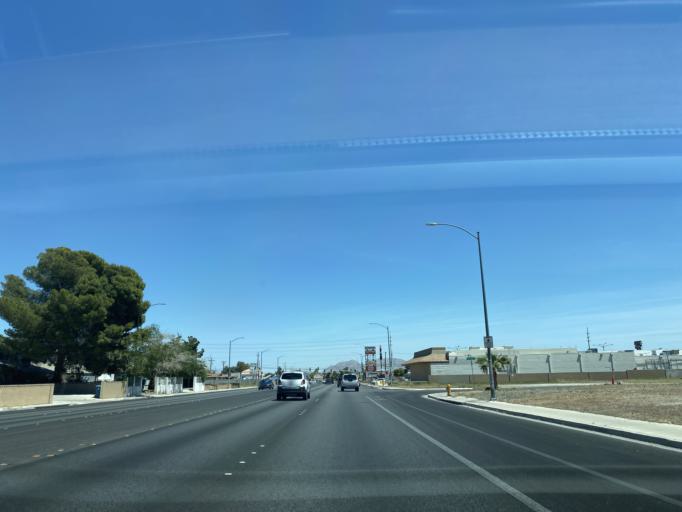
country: US
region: Nevada
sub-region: Clark County
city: Las Vegas
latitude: 36.1955
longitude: -115.2090
